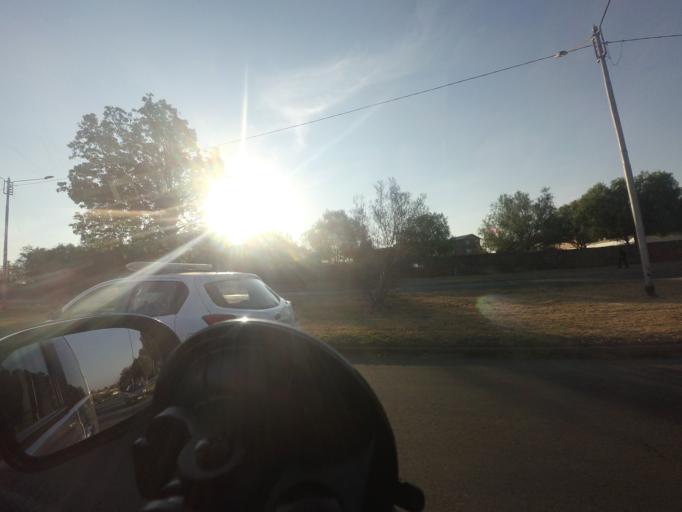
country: ZA
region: Gauteng
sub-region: Sedibeng District Municipality
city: Vereeniging
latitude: -26.6591
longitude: 27.9534
